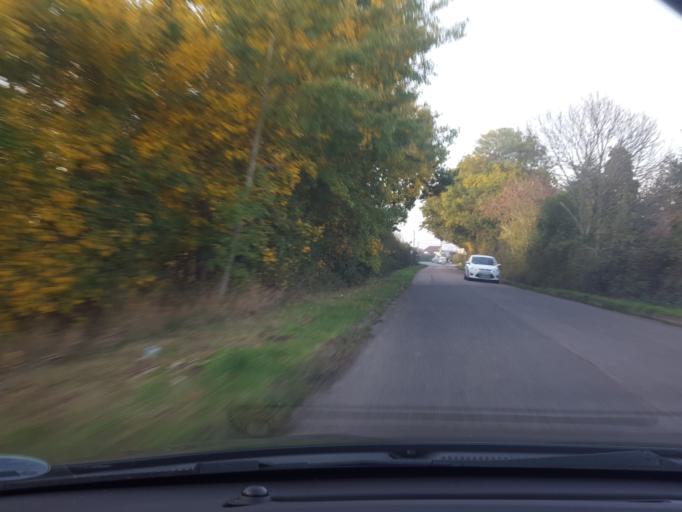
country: GB
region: England
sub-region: Essex
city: Little Clacton
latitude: 51.8408
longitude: 1.1232
